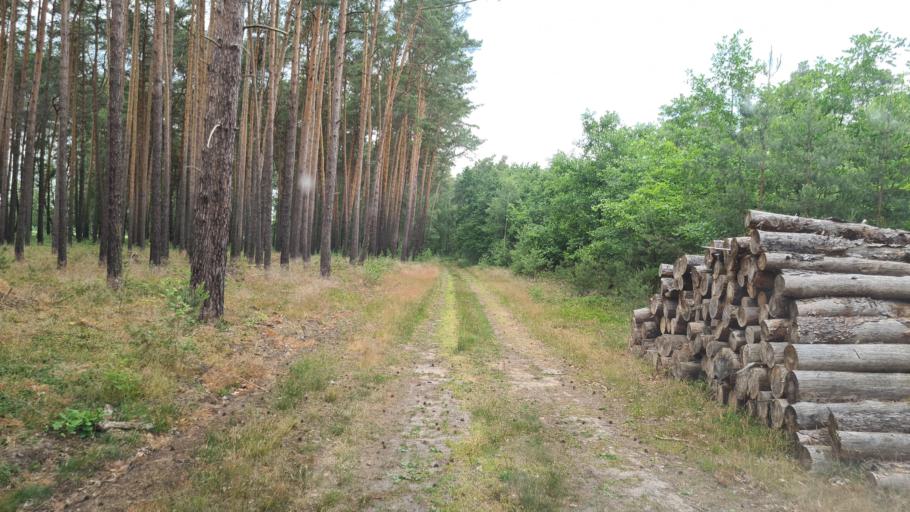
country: DE
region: Brandenburg
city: Crinitz
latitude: 51.6816
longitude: 13.7427
